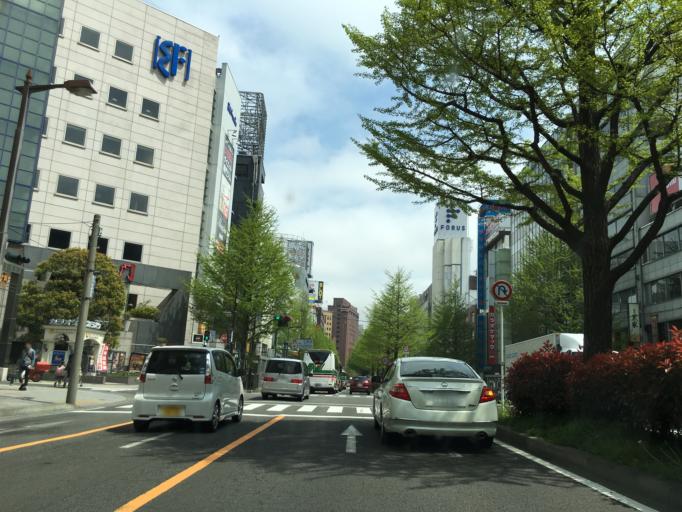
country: JP
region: Miyagi
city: Sendai
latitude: 38.2622
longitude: 140.8697
